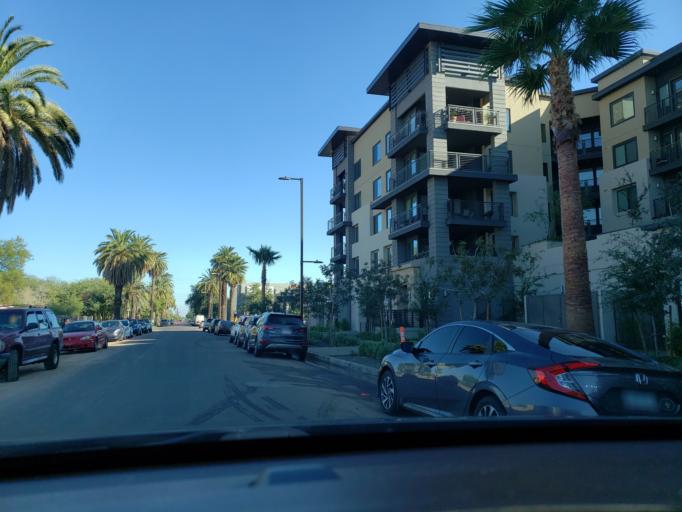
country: US
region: Arizona
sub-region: Maricopa County
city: Phoenix
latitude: 33.4600
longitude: -112.0687
